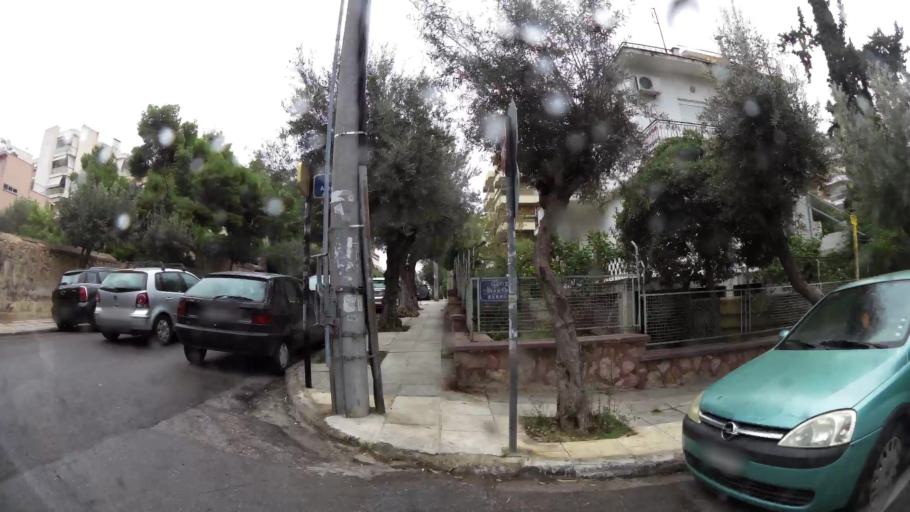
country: GR
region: Attica
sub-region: Nomarchia Athinas
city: Palaio Faliro
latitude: 37.9244
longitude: 23.7026
